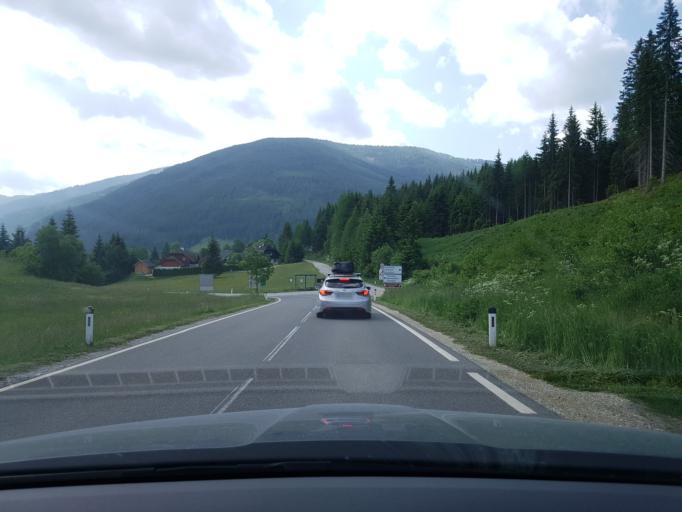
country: AT
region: Salzburg
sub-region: Politischer Bezirk Tamsweg
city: Thomatal
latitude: 47.0821
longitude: 13.7226
